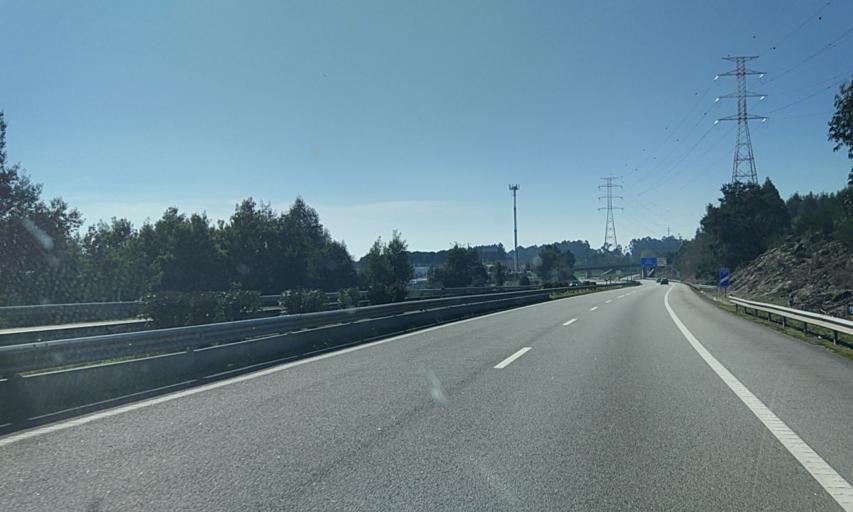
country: PT
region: Porto
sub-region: Paredes
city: Baltar
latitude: 41.1734
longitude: -8.3835
